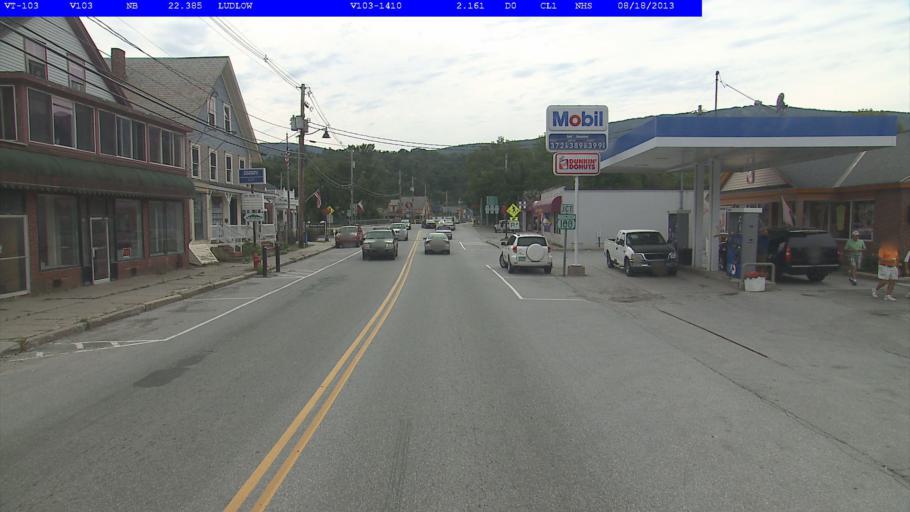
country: US
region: Vermont
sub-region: Windsor County
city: Chester
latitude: 43.3961
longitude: -72.7013
